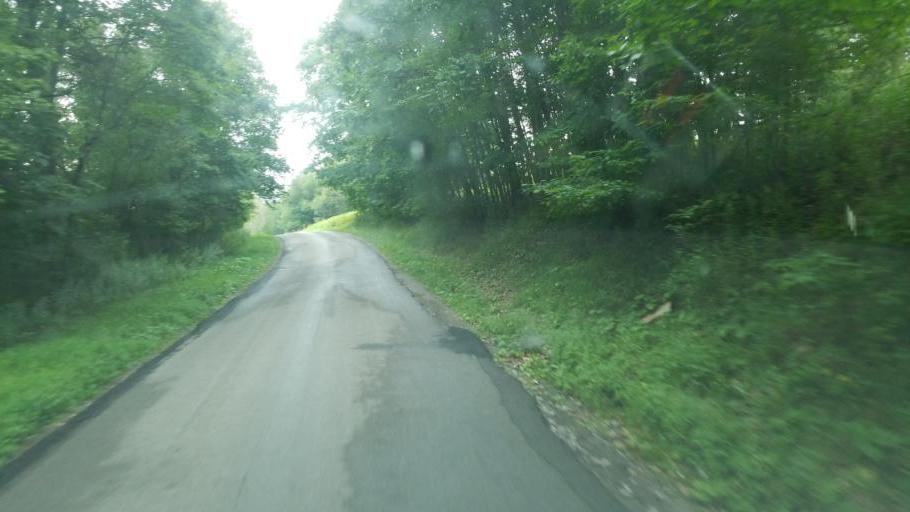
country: US
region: Pennsylvania
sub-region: Clarion County
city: Clarion
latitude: 41.1771
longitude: -79.3810
